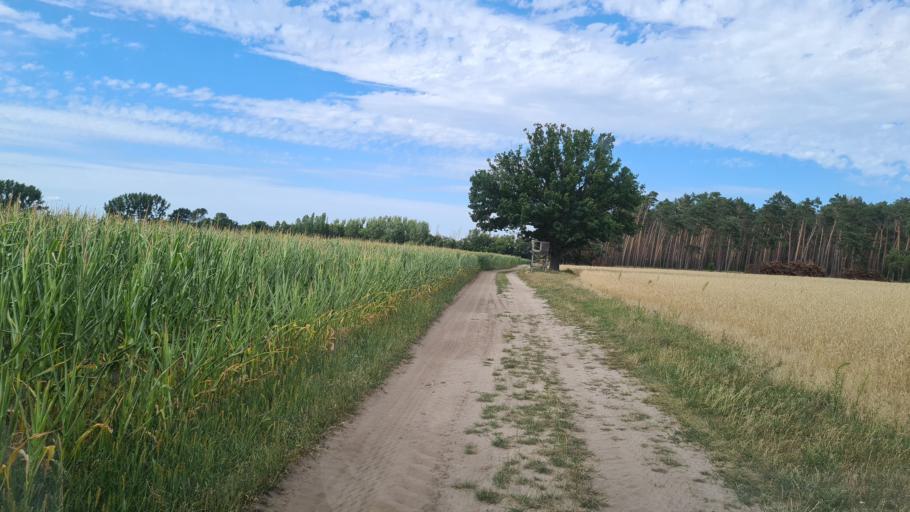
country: DE
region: Saxony-Anhalt
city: Holzdorf
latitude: 51.8220
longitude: 13.1967
